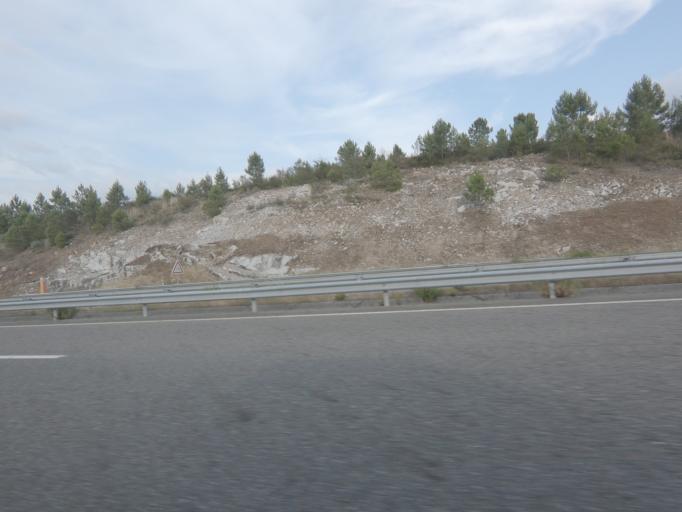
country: PT
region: Vila Real
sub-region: Boticas
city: Boticas
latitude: 41.6360
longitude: -7.5945
